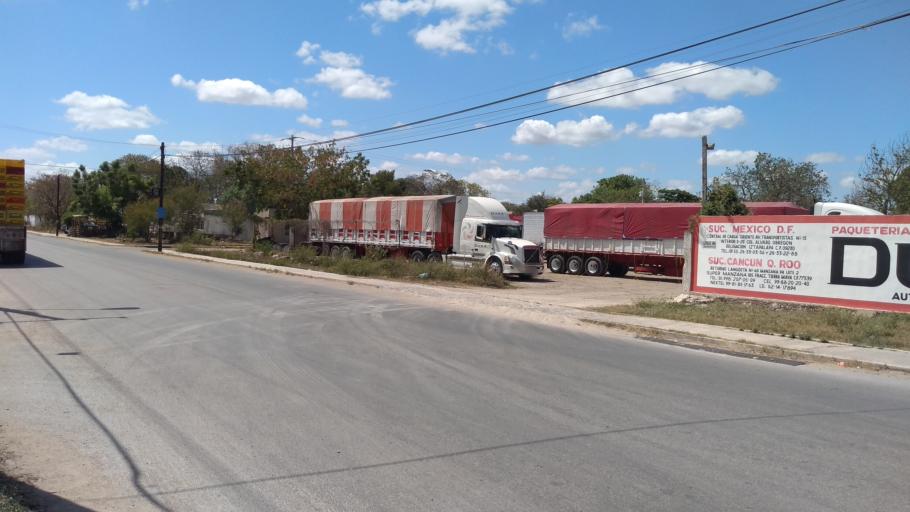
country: MX
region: Yucatan
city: Itzincab Palomeque
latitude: 20.9231
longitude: -89.6705
